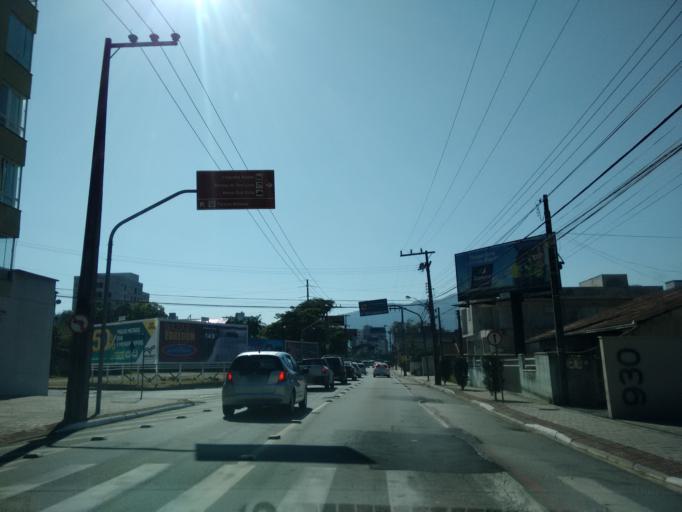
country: BR
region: Santa Catarina
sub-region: Jaragua Do Sul
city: Jaragua do Sul
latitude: -26.4983
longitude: -49.0809
